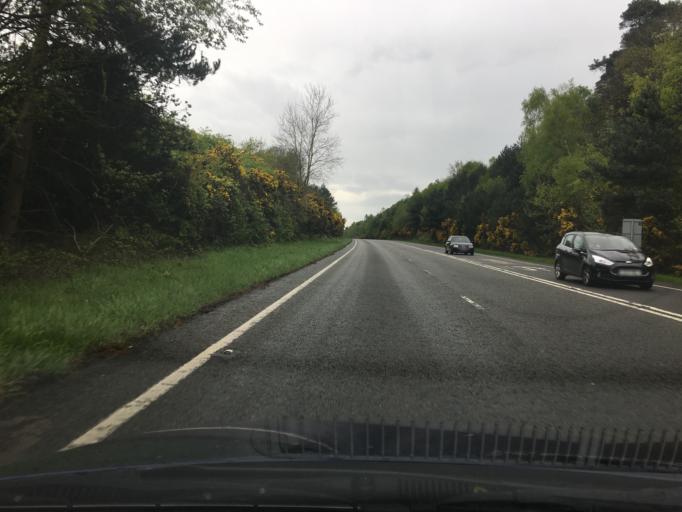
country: GB
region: England
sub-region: Bracknell Forest
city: Sandhurst
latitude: 51.3610
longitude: -0.7711
